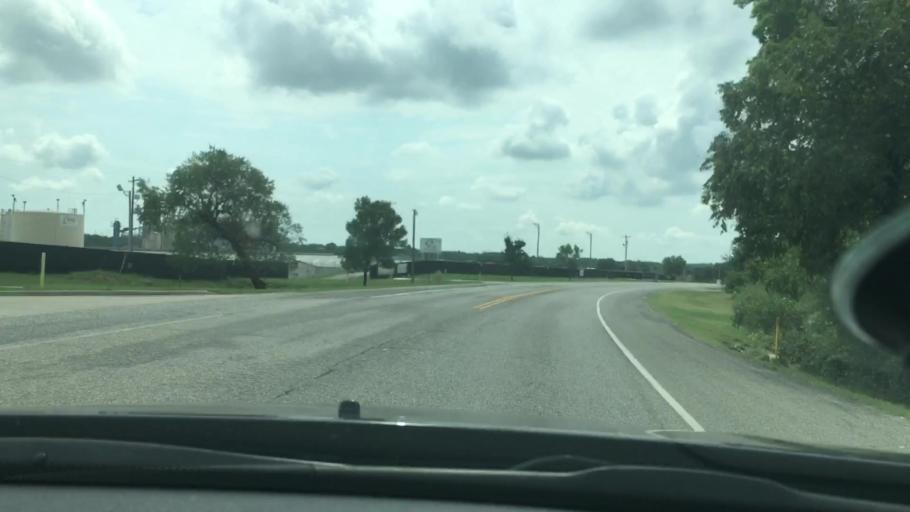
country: US
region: Oklahoma
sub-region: Carter County
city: Ardmore
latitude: 34.2009
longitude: -97.1090
